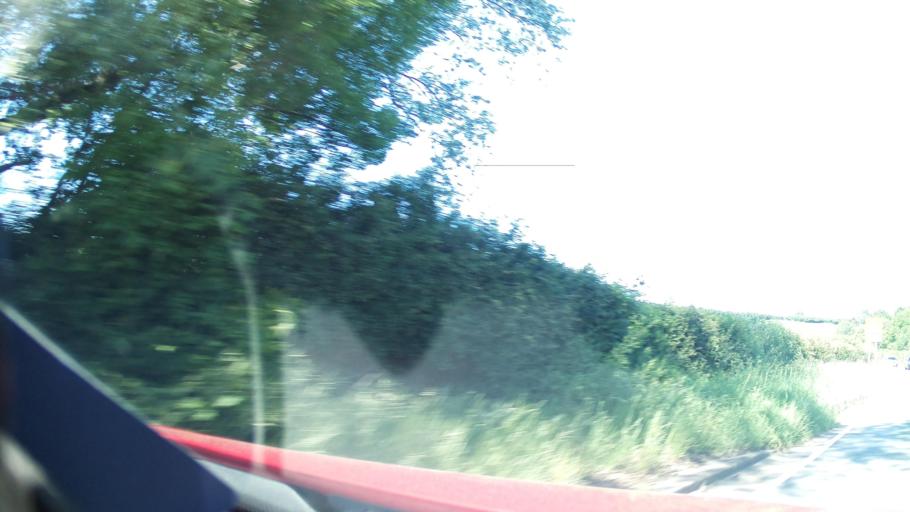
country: GB
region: England
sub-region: Somerset
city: Stoke-sub-Hamdon
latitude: 50.9063
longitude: -2.7462
